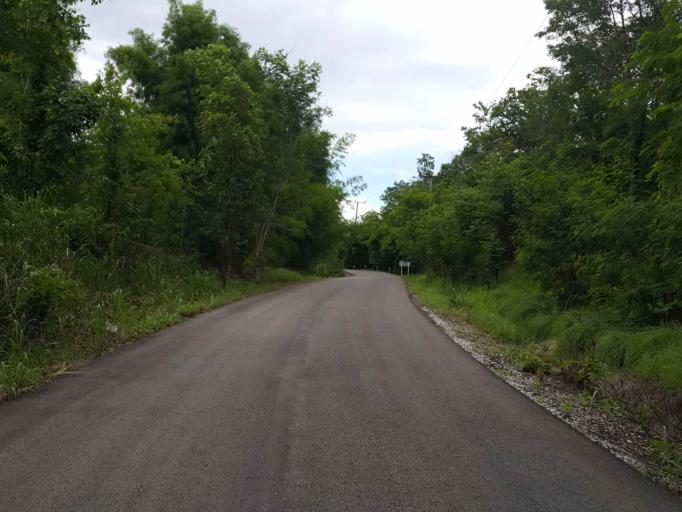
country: TH
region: Chiang Mai
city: San Sai
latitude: 18.9372
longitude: 98.9180
